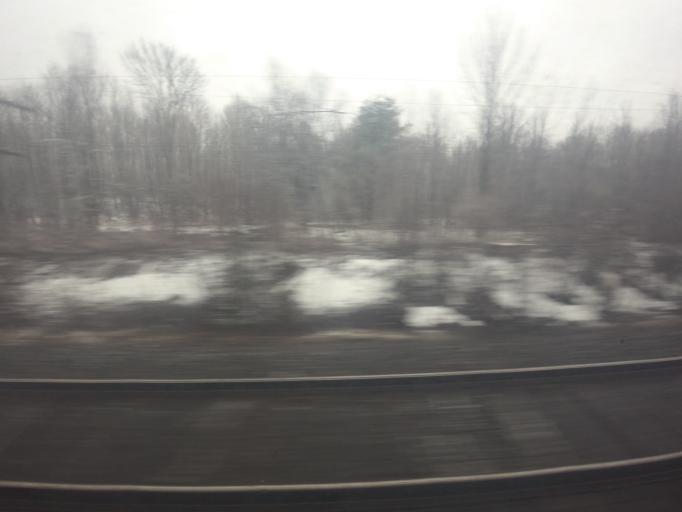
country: CA
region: Ontario
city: Brockville
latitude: 44.5721
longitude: -75.7534
